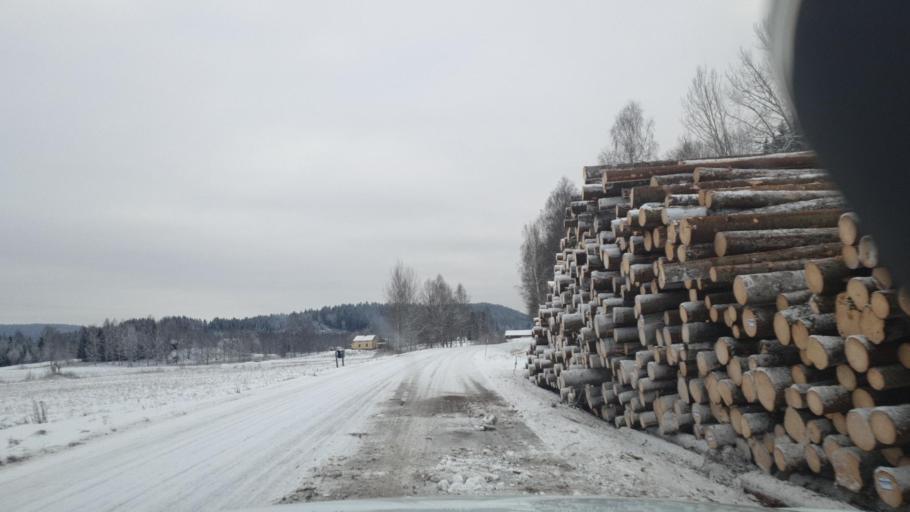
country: NO
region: Ostfold
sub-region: Romskog
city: Romskog
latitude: 59.8050
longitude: 12.0087
